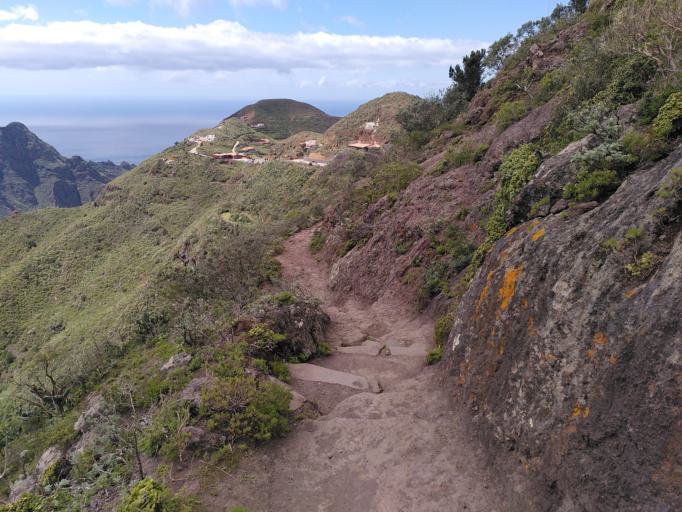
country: ES
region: Canary Islands
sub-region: Provincia de Santa Cruz de Tenerife
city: Tegueste
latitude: 28.5601
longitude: -16.2867
